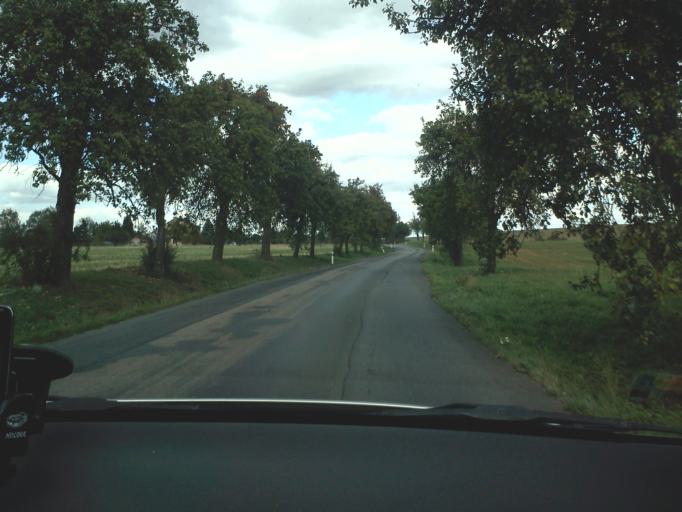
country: CZ
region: Central Bohemia
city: Cesky Brod
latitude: 50.0923
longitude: 14.8646
